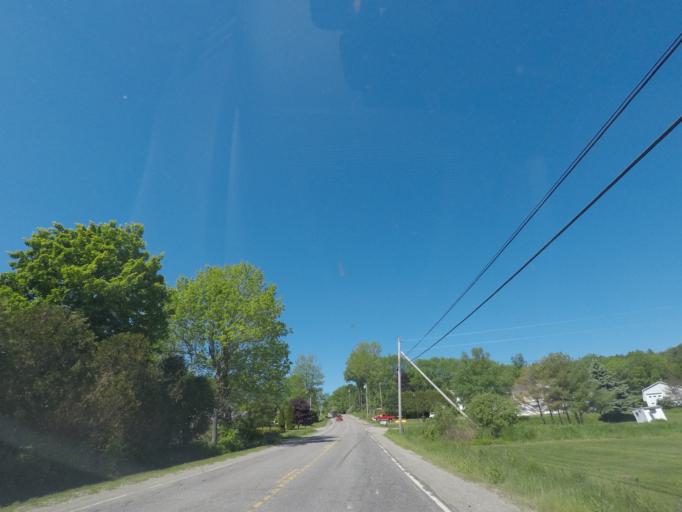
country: US
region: Maine
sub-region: Kennebec County
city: Gardiner
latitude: 44.2307
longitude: -69.8152
